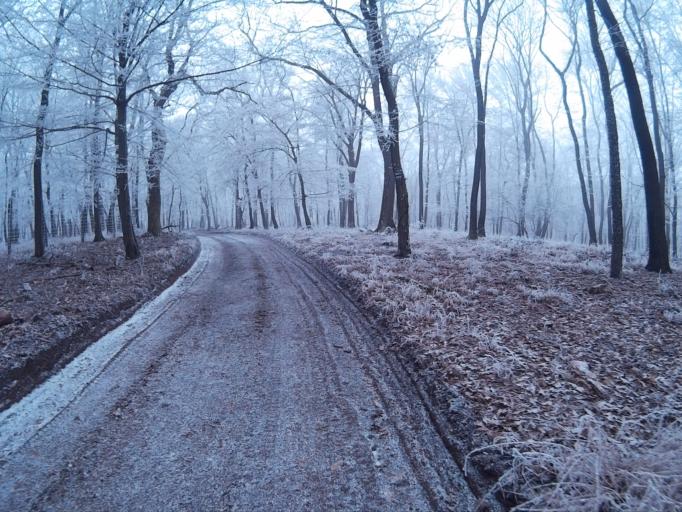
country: HU
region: Komarom-Esztergom
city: Oroszlany
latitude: 47.4404
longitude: 18.3766
